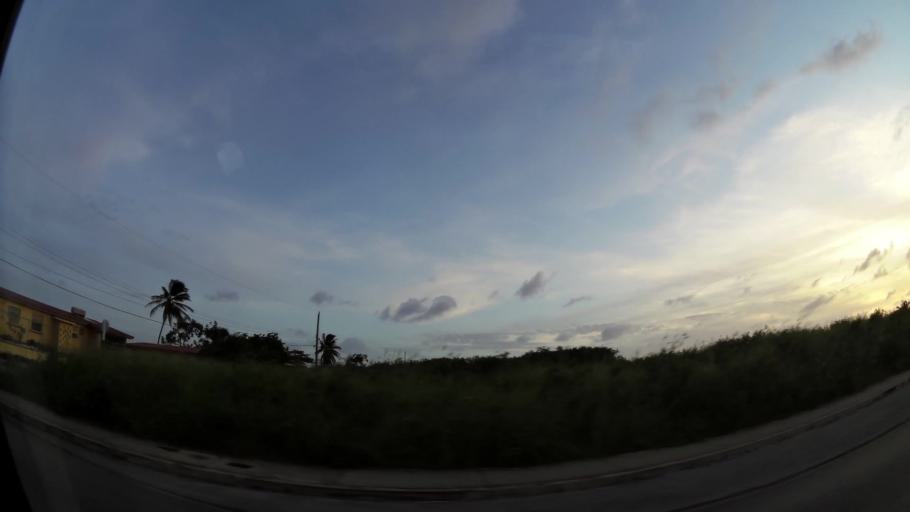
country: BB
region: Saint Philip
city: Crane
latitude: 13.1049
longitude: -59.4625
